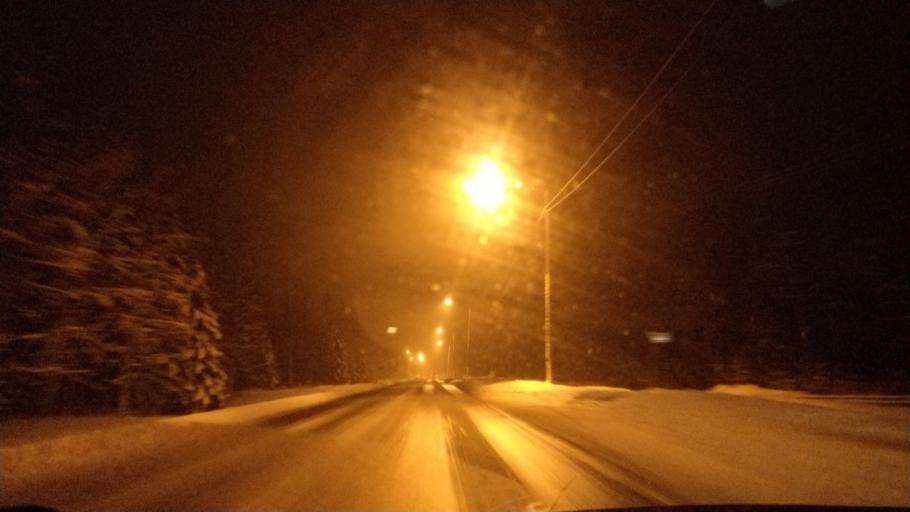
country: FI
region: Lapland
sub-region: Rovaniemi
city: Rovaniemi
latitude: 66.2787
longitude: 25.3338
